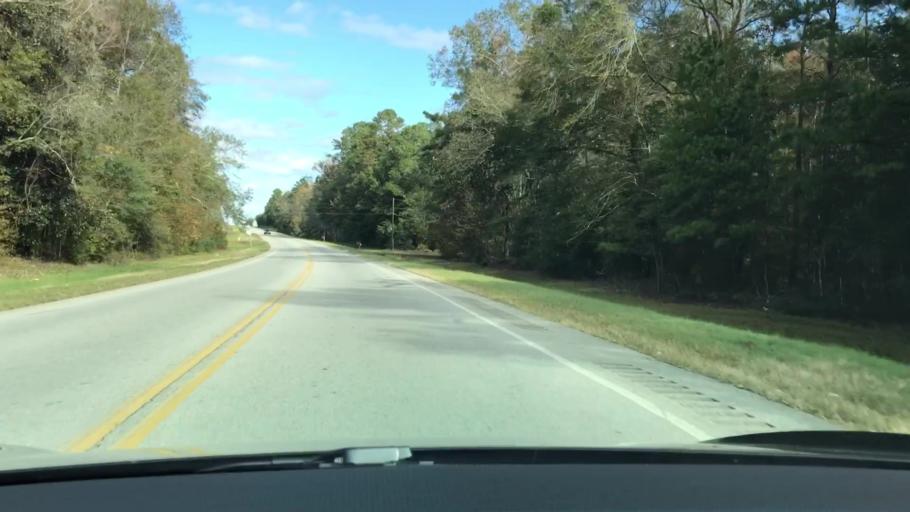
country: US
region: Georgia
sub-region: Jefferson County
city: Louisville
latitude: 32.9754
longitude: -82.3905
